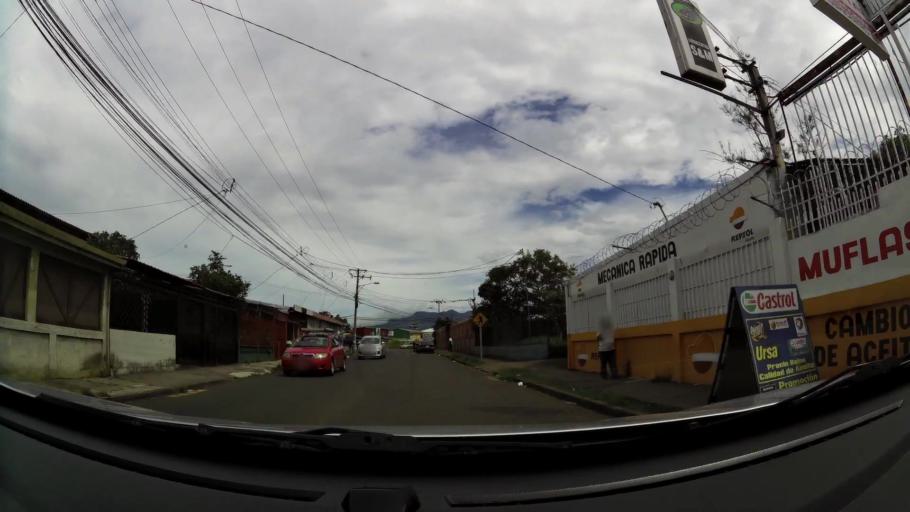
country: CR
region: San Jose
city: San Rafael Arriba
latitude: 9.9017
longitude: -84.0737
